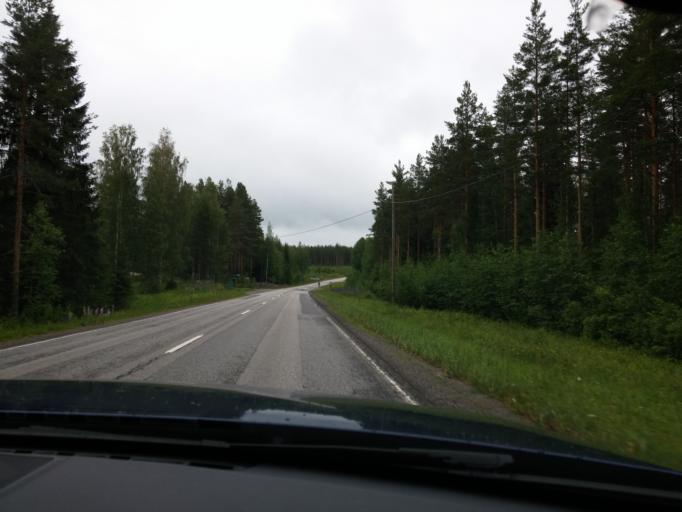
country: FI
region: Central Finland
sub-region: Keuruu
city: Keuruu
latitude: 62.3301
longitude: 24.7329
